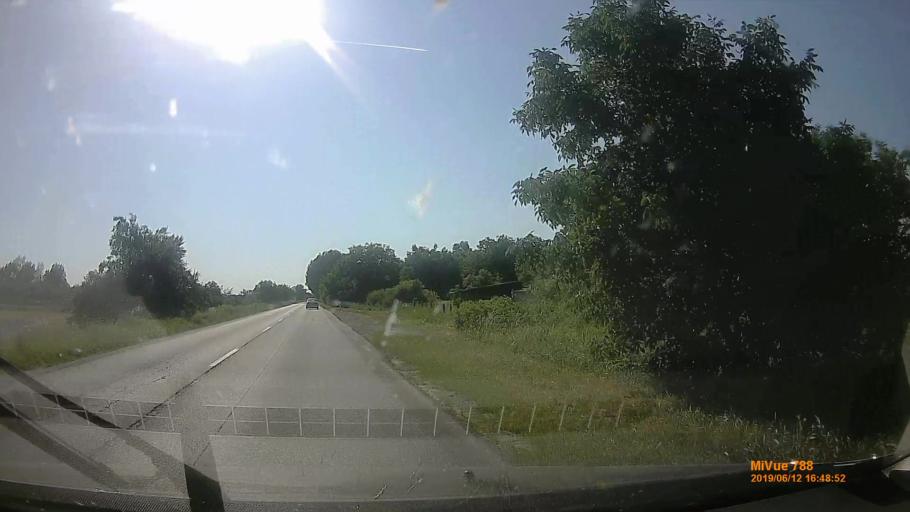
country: HU
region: Csongrad
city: Kiszombor
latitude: 46.1922
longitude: 20.4209
